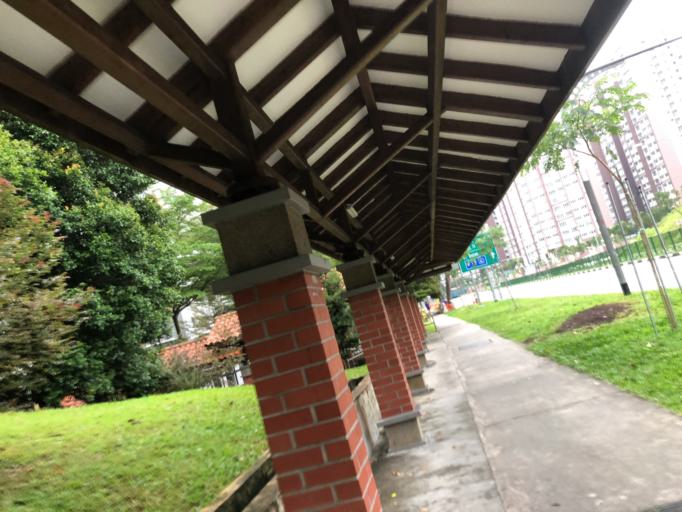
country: MY
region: Johor
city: Johor Bahru
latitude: 1.3522
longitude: 103.7467
